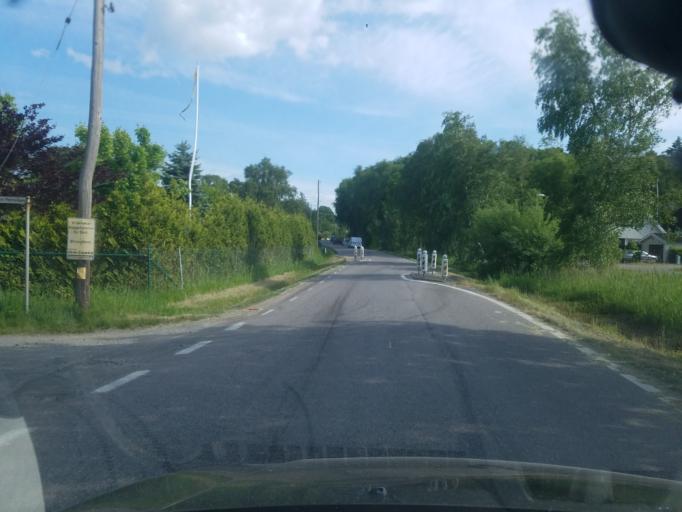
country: SE
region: Halland
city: Saro
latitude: 57.5158
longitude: 11.9496
